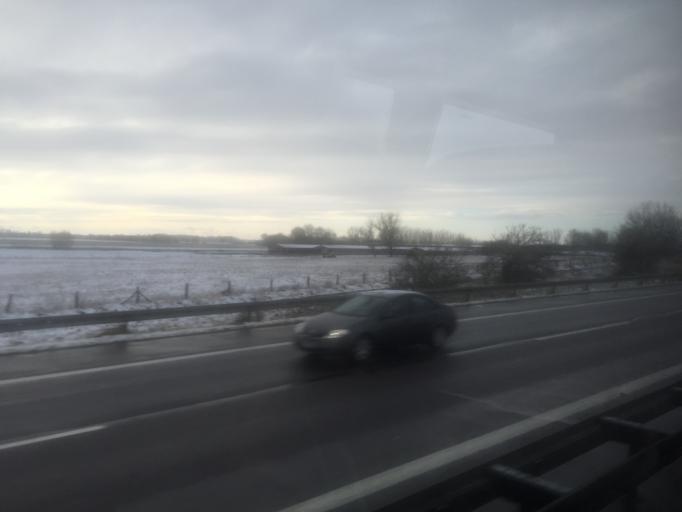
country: DE
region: Brandenburg
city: Fehrbellin
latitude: 52.7503
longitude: 12.8739
